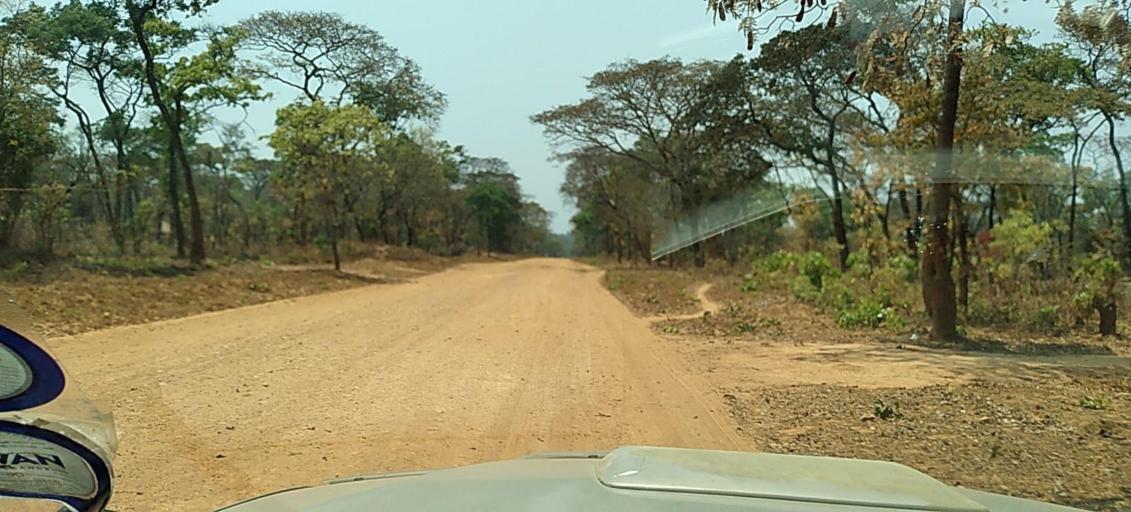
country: ZM
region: North-Western
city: Kasempa
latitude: -13.5474
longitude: 26.0350
